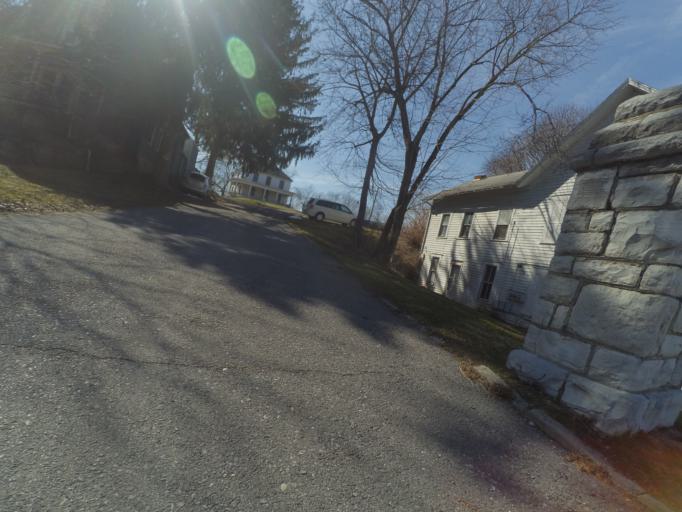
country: US
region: Pennsylvania
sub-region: Centre County
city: Bellefonte
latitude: 40.9097
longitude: -77.7790
